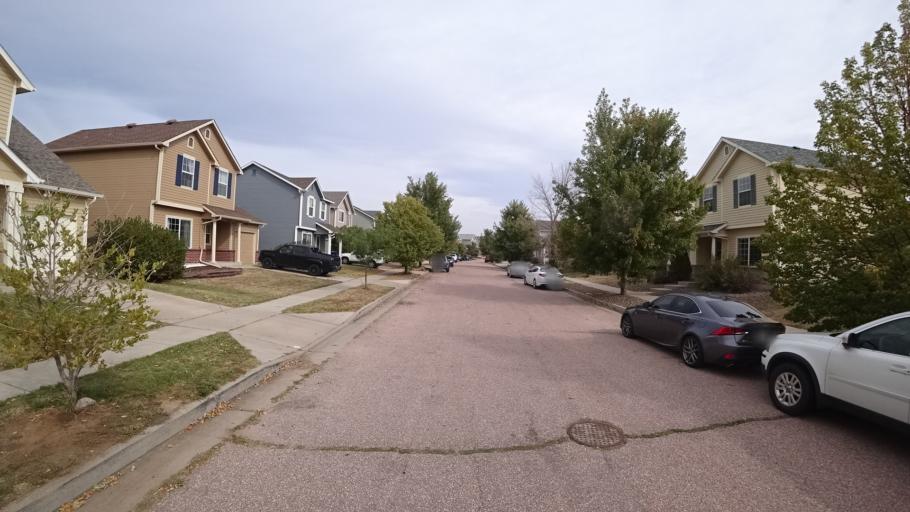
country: US
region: Colorado
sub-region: El Paso County
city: Cimarron Hills
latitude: 38.9214
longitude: -104.7165
